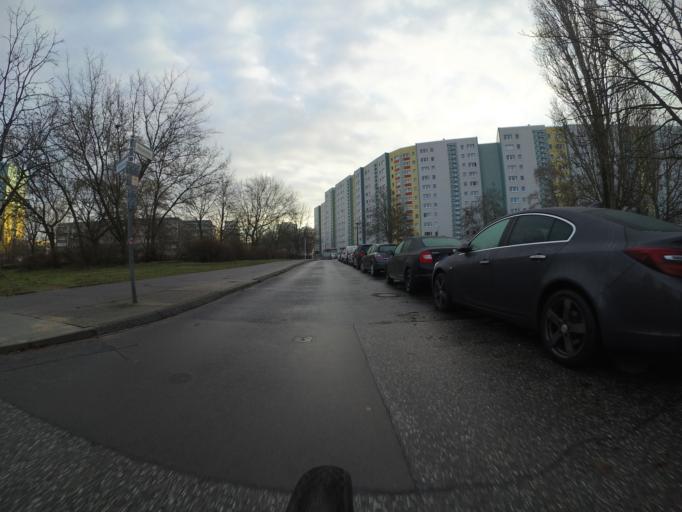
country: DE
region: Berlin
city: Marzahn
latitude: 52.5389
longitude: 13.5527
